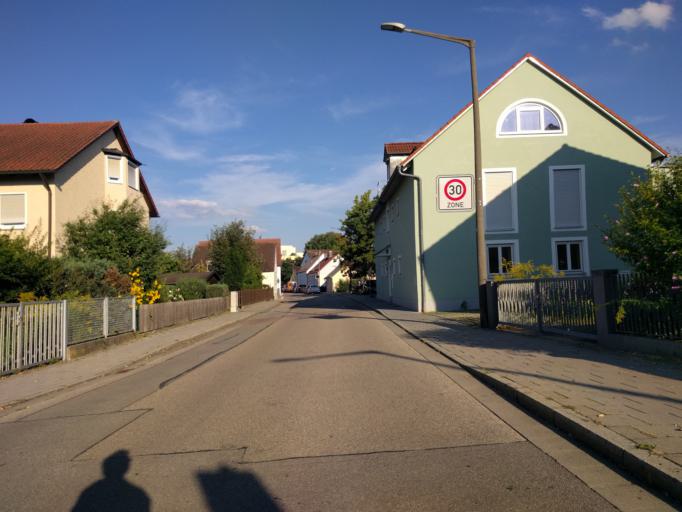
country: DE
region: Bavaria
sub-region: Upper Palatinate
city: Regensburg
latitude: 49.0239
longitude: 12.1176
